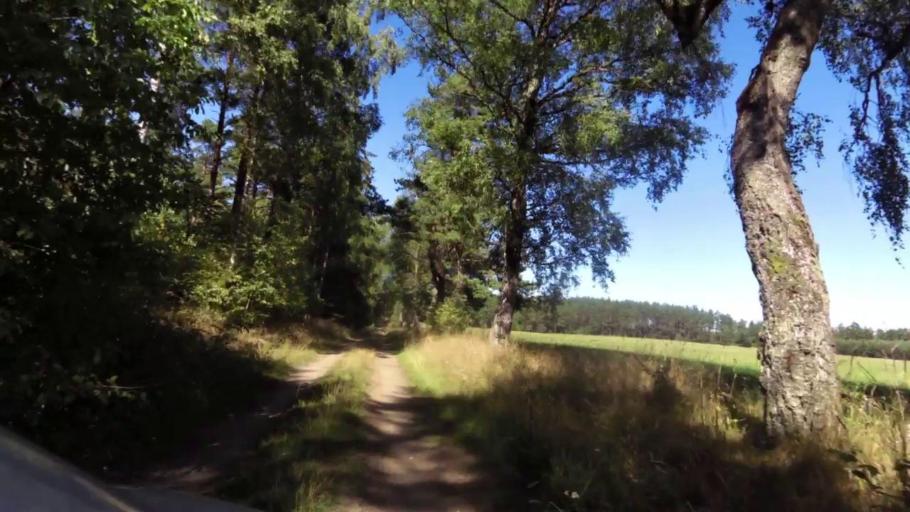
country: PL
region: West Pomeranian Voivodeship
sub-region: Powiat szczecinecki
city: Bialy Bor
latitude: 53.8255
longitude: 16.8673
